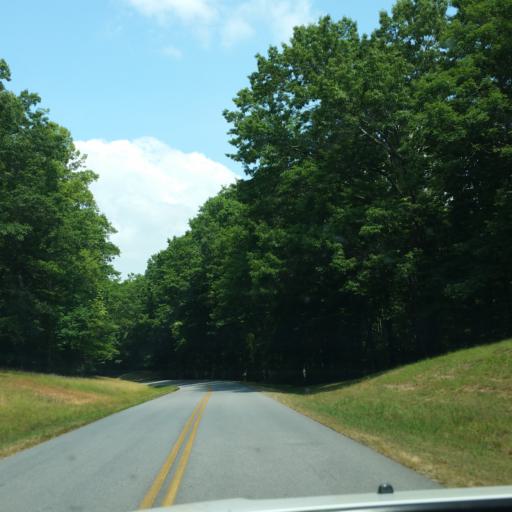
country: US
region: North Carolina
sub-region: Buncombe County
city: Bent Creek
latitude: 35.4987
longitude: -82.5731
